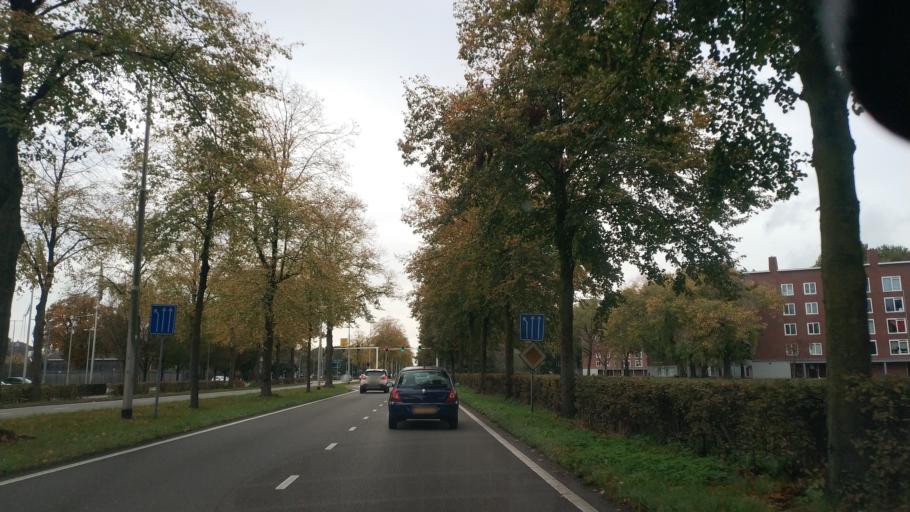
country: NL
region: North Brabant
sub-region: Gemeente Tilburg
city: Tilburg
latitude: 51.5441
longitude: 5.0739
